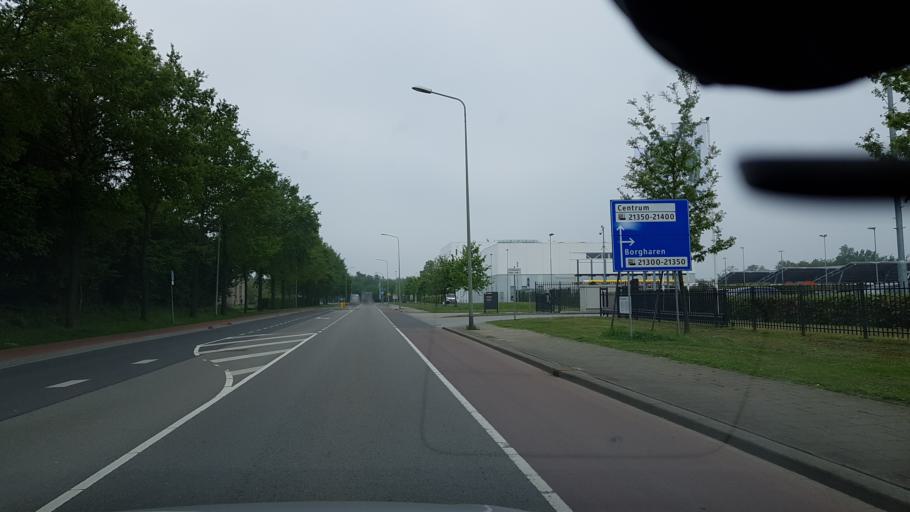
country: NL
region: Limburg
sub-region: Gemeente Maastricht
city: Maastricht
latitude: 50.8698
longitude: 5.7057
